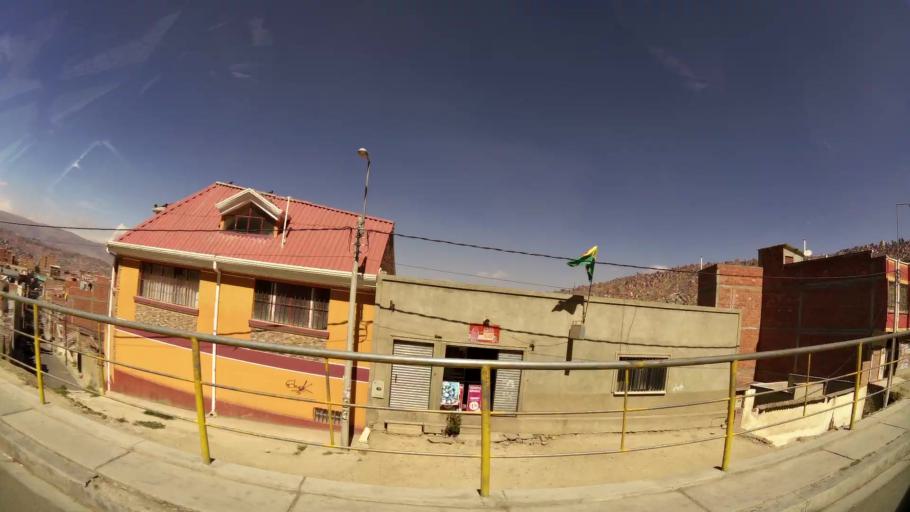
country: BO
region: La Paz
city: La Paz
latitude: -16.4894
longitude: -68.1540
